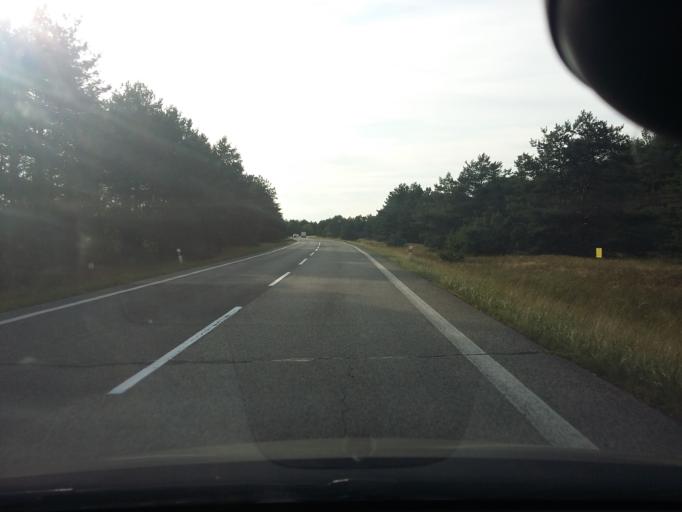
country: SK
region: Bratislavsky
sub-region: Okres Malacky
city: Malacky
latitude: 48.4067
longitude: 17.0779
